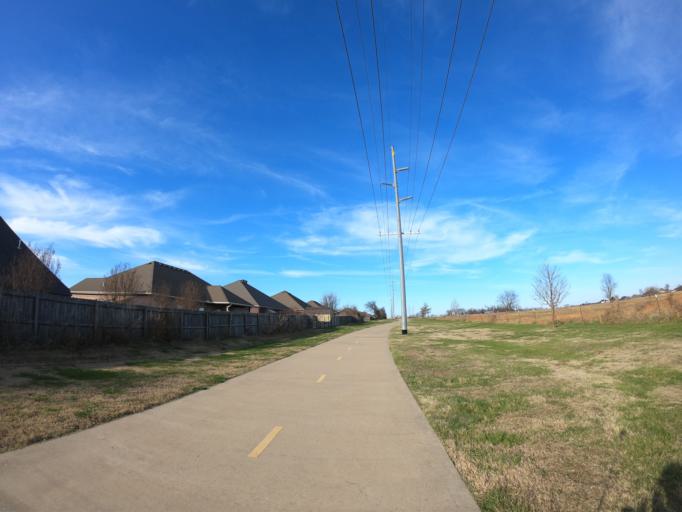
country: US
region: Arkansas
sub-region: Benton County
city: Lowell
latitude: 36.2715
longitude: -94.1677
